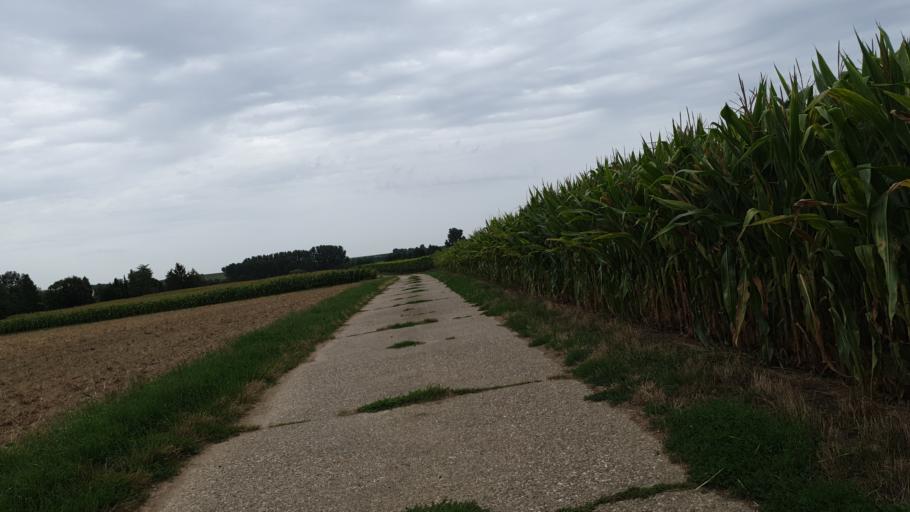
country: DE
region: Rheinland-Pfalz
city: Barbelroth
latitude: 49.1080
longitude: 8.0681
